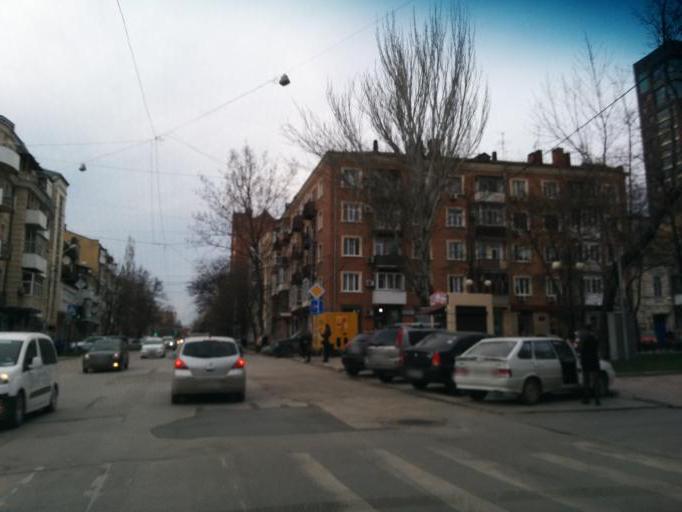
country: RU
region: Rostov
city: Rostov-na-Donu
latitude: 47.2258
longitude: 39.7205
